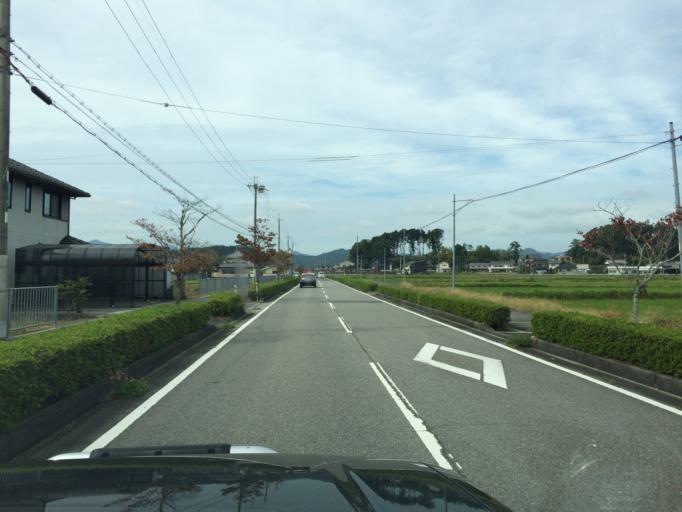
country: JP
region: Hyogo
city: Sasayama
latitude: 35.0722
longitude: 135.1939
